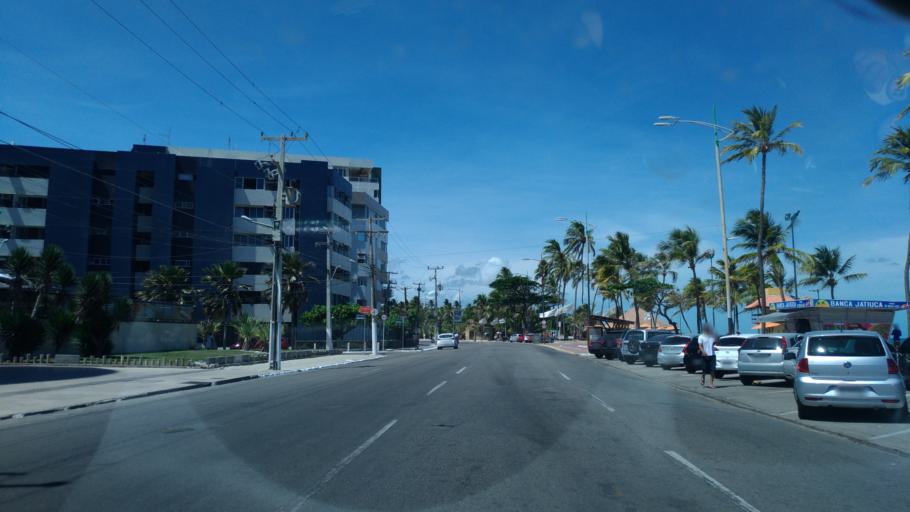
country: BR
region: Alagoas
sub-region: Maceio
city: Maceio
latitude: -9.6451
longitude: -35.6996
